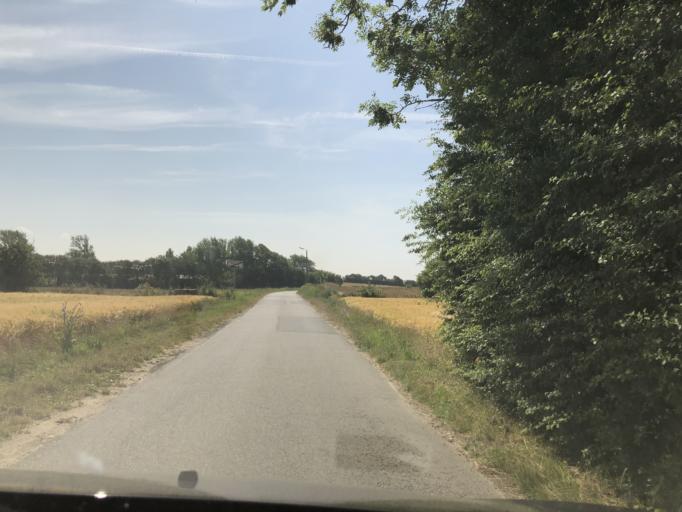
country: DK
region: South Denmark
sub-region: Faaborg-Midtfyn Kommune
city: Faaborg
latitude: 54.9540
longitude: 10.2261
